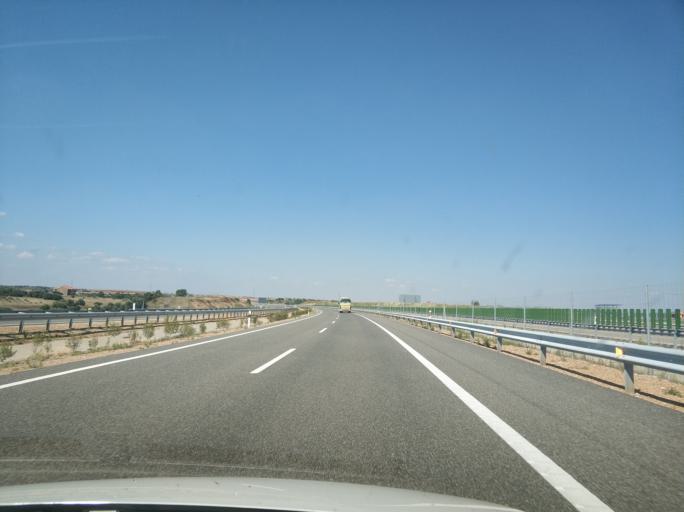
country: ES
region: Castille and Leon
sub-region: Provincia de Zamora
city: San Cebrian de Castro
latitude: 41.6958
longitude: -5.7962
